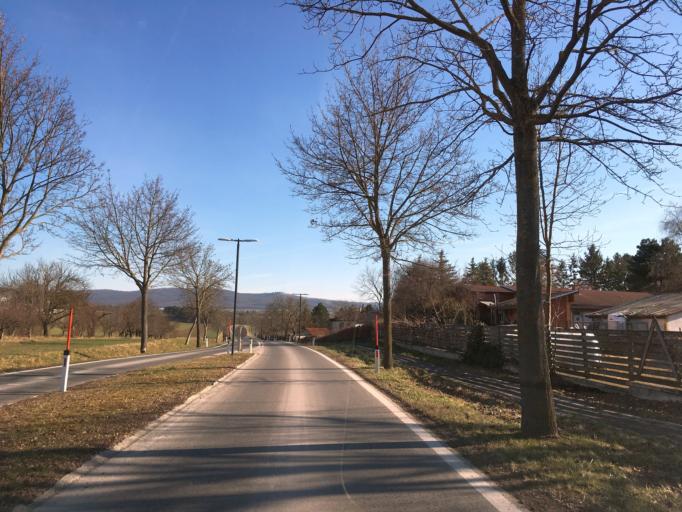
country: AT
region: Burgenland
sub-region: Eisenstadt-Umgebung
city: Wimpassing an der Leitha
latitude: 47.9128
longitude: 16.4280
